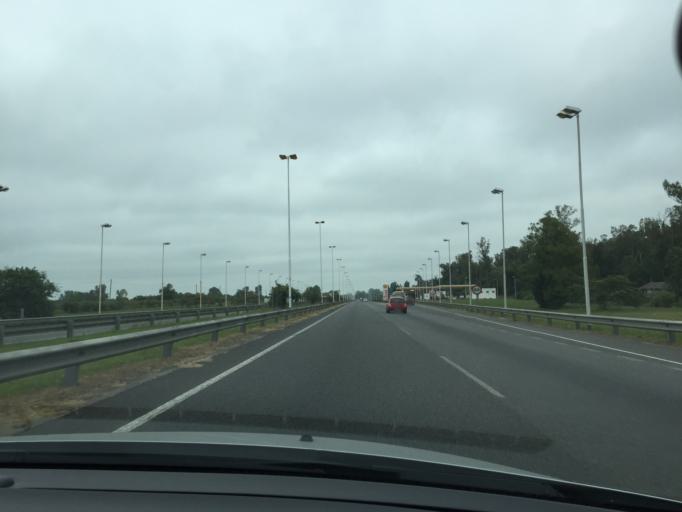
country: AR
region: Buenos Aires
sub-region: Partido de Ezeiza
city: Ezeiza
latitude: -34.8589
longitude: -58.5614
